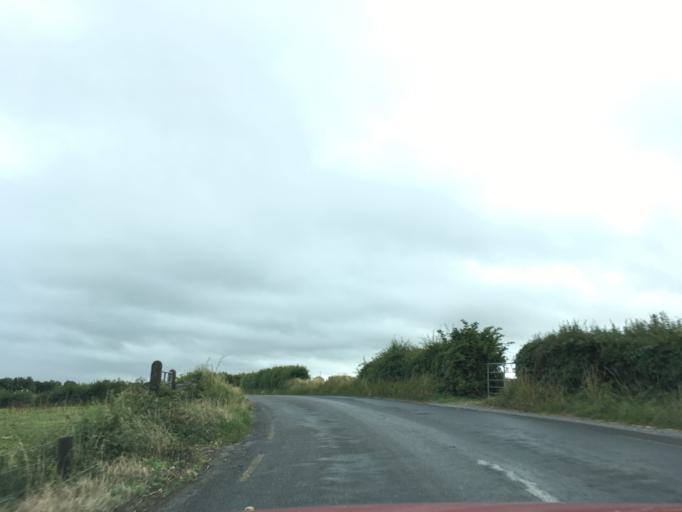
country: IE
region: Munster
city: Cashel
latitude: 52.4530
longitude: -7.8159
